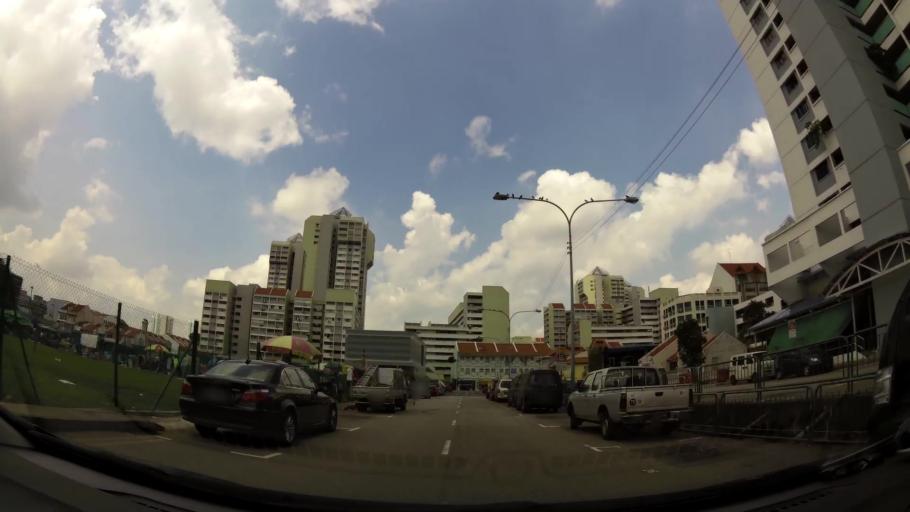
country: SG
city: Singapore
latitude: 1.3053
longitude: 103.8568
